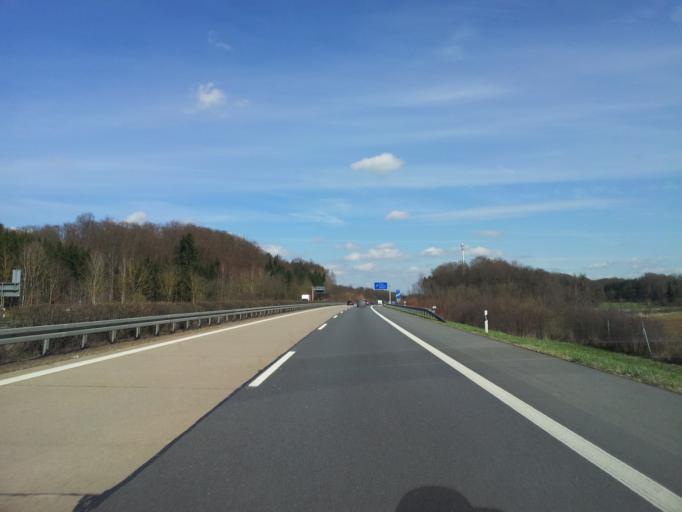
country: DE
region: Baden-Wuerttemberg
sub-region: Regierungsbezirk Stuttgart
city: Buch am Ahorn
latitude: 49.5372
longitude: 9.5838
